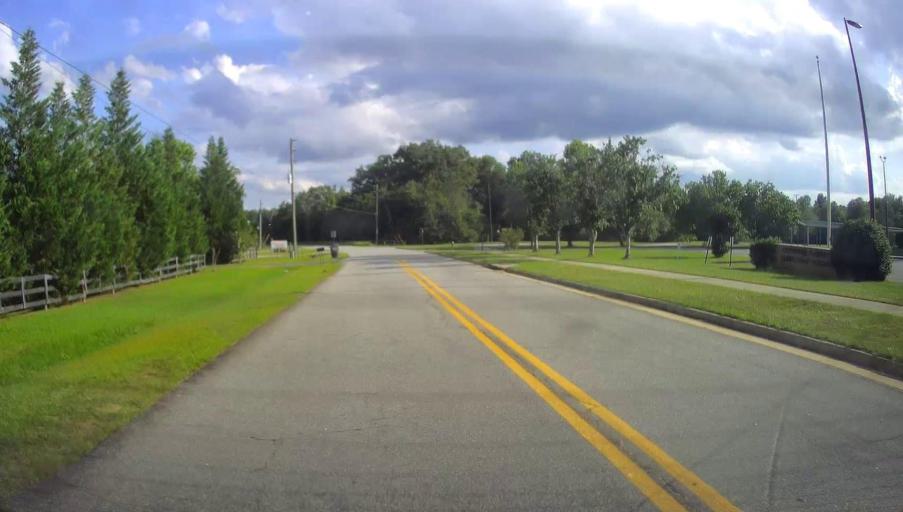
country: US
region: Georgia
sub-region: Crawford County
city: Roberta
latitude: 32.7284
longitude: -84.0065
